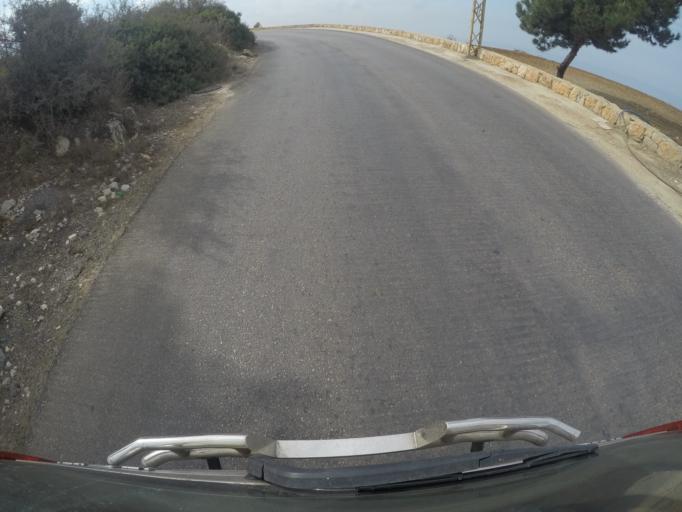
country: LB
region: Mont-Liban
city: Beit ed Dine
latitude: 33.7343
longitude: 35.4751
